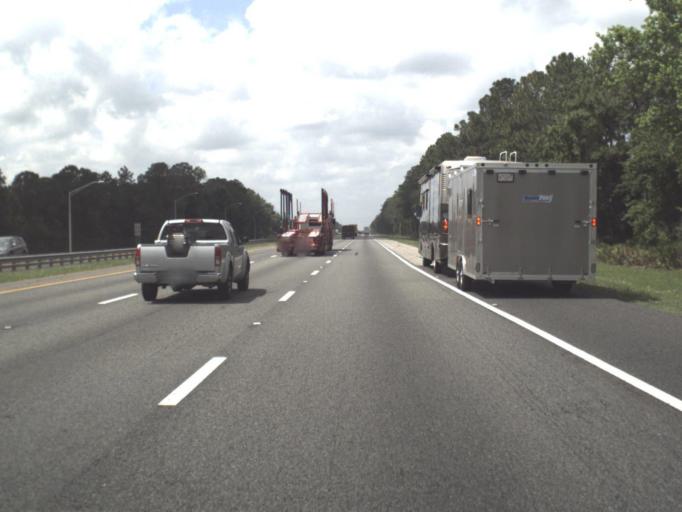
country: US
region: Florida
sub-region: Saint Johns County
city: Saint Augustine Shores
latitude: 29.7088
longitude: -81.3307
